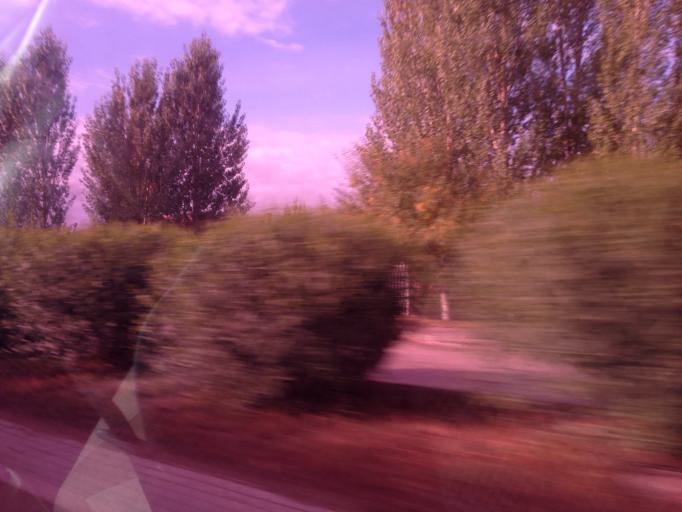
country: KZ
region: Astana Qalasy
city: Astana
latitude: 51.1453
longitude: 71.4448
